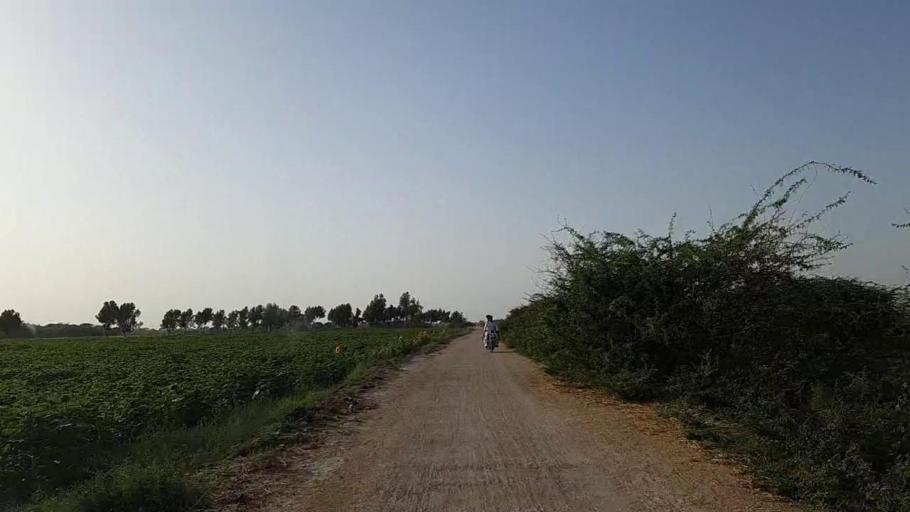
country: PK
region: Sindh
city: Jati
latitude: 24.3287
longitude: 68.1607
